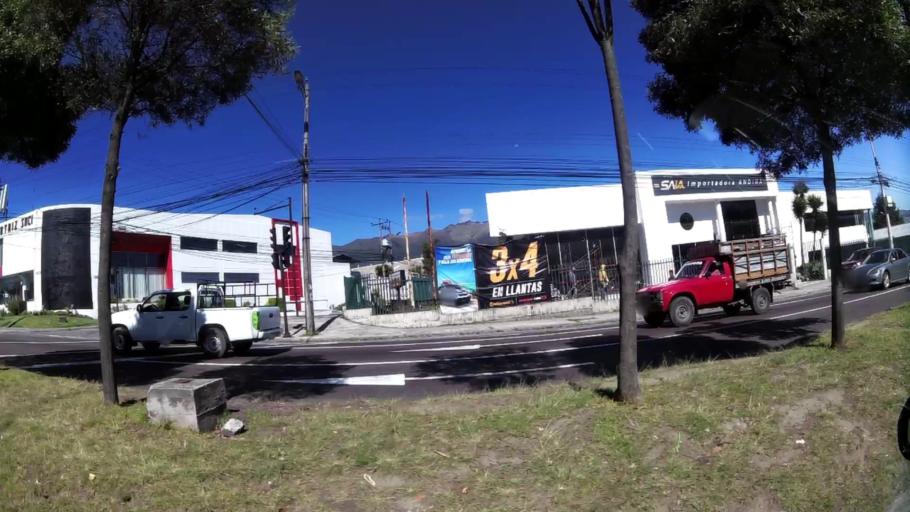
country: EC
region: Pichincha
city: Quito
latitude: -0.1263
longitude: -78.4782
